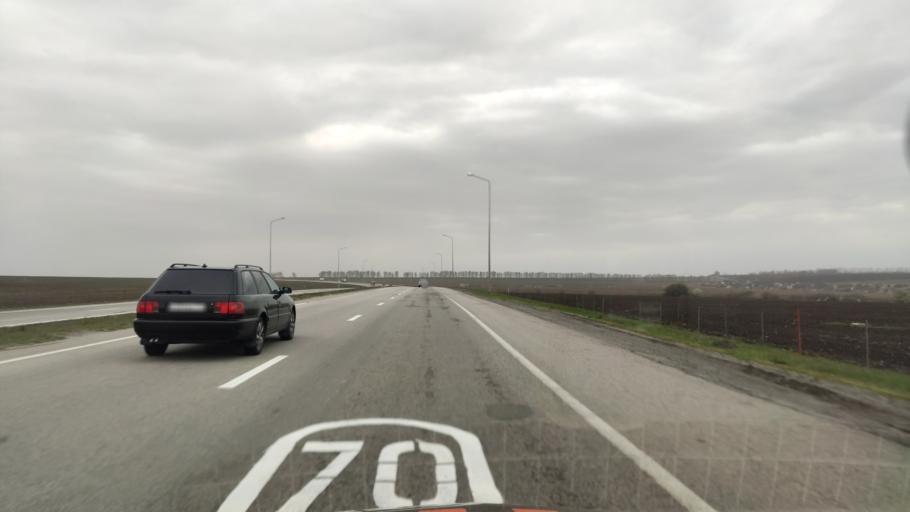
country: RU
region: Belgorod
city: Staryy Oskol
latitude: 51.3392
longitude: 37.7794
